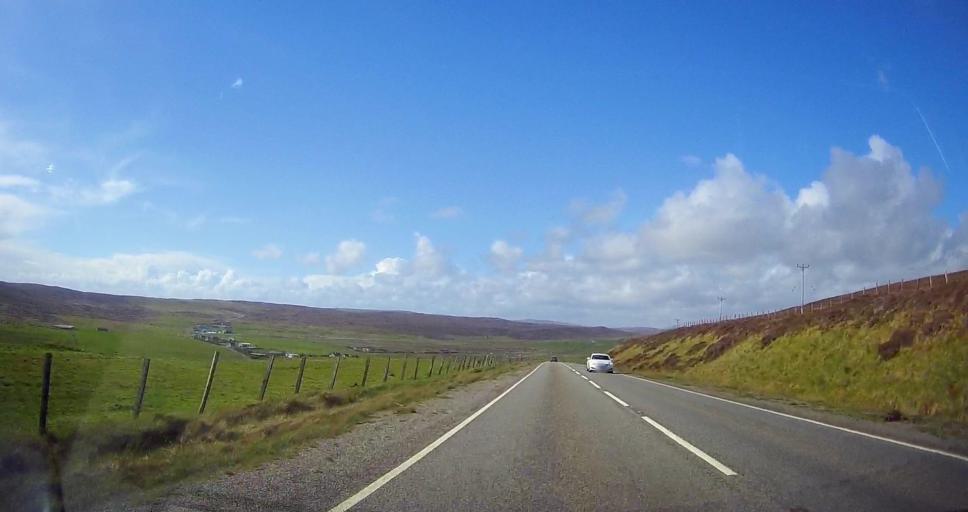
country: GB
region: Scotland
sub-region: Shetland Islands
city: Lerwick
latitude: 60.1776
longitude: -1.2236
